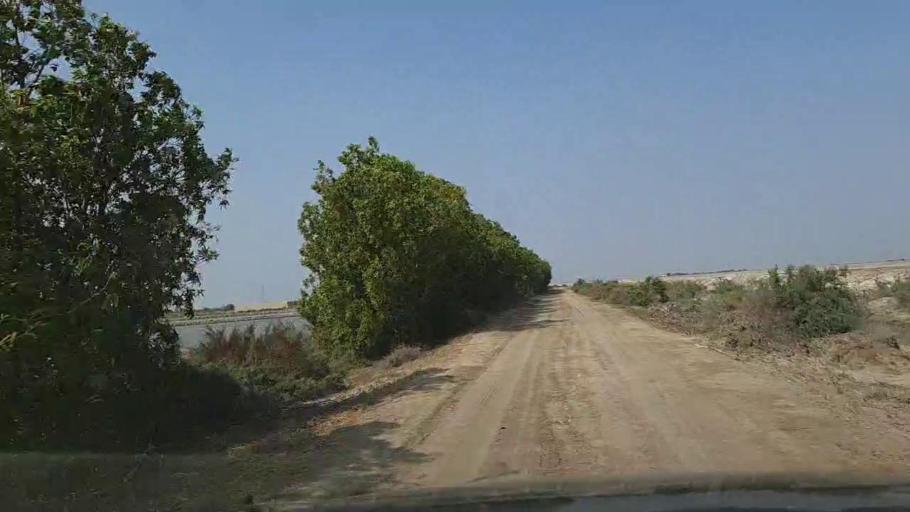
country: PK
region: Sindh
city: Gharo
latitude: 24.7058
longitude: 67.5580
